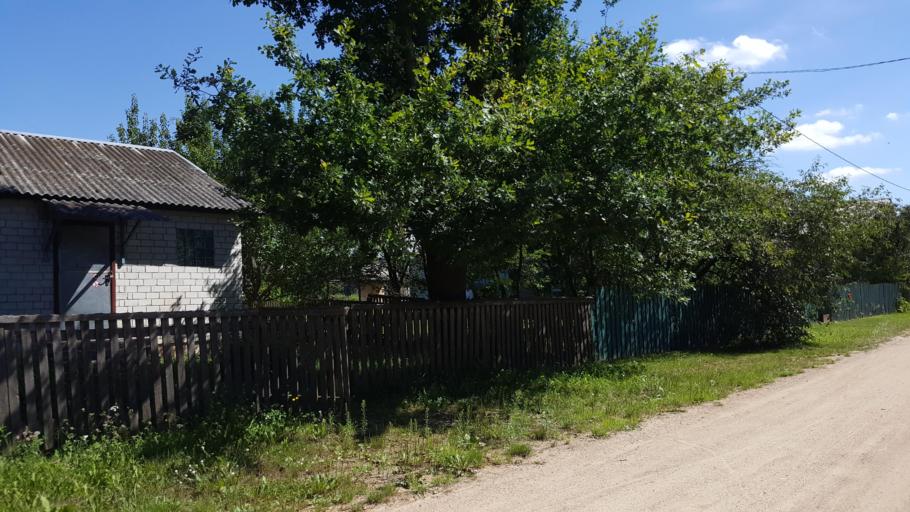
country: BY
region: Brest
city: Charnawchytsy
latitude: 52.3670
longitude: 23.6243
